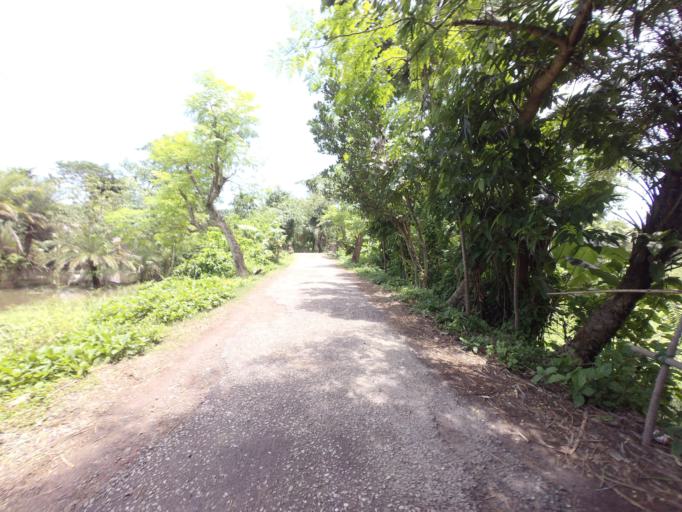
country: BD
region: Khulna
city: Kalia
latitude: 23.0462
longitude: 89.6460
